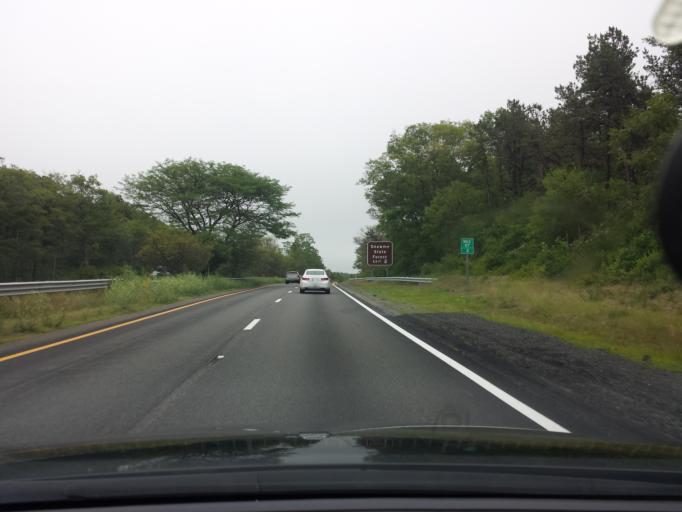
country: US
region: Massachusetts
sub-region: Barnstable County
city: Sagamore
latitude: 41.7533
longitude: -70.5184
